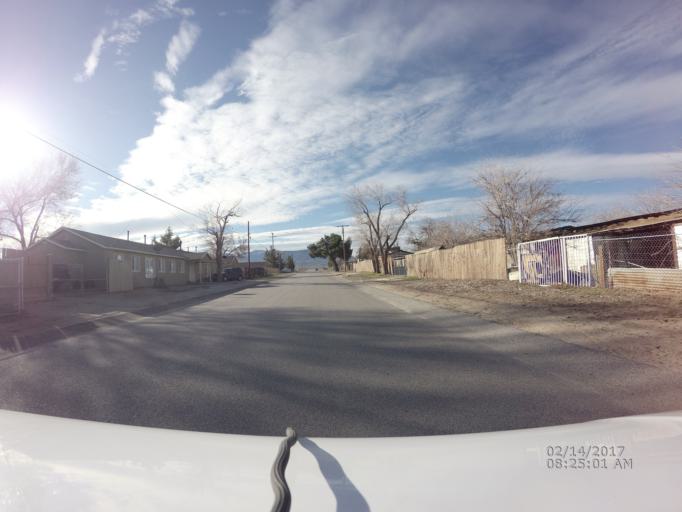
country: US
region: California
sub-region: Los Angeles County
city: Littlerock
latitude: 34.5455
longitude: -117.9494
